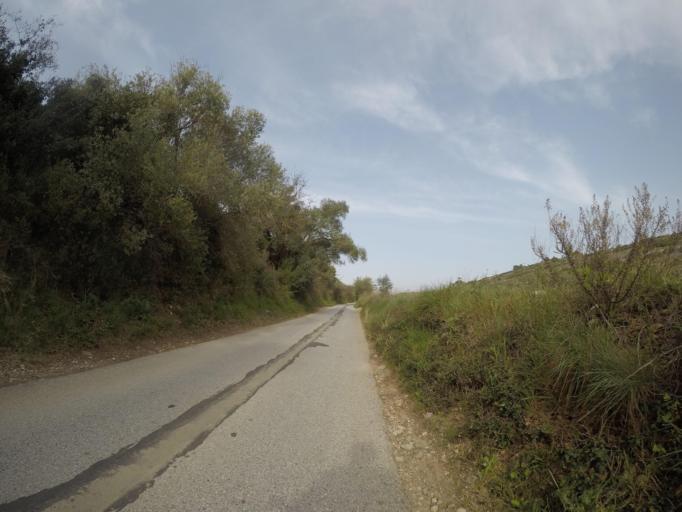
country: FR
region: Languedoc-Roussillon
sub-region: Departement des Pyrenees-Orientales
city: Baixas
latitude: 42.7666
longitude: 2.8131
